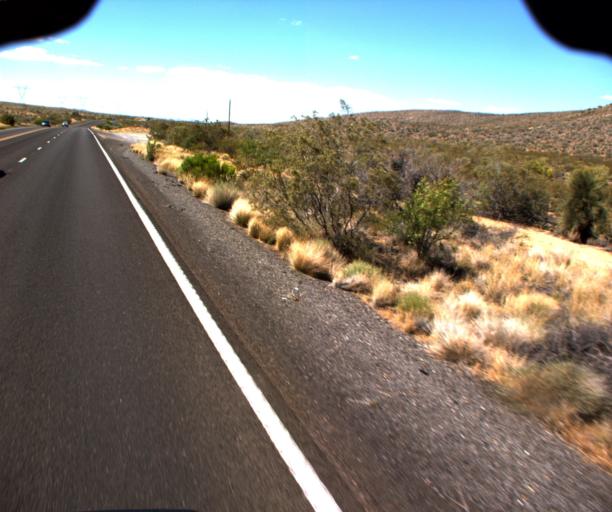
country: US
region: Arizona
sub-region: Mohave County
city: Kingman
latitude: 34.9399
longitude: -113.6643
